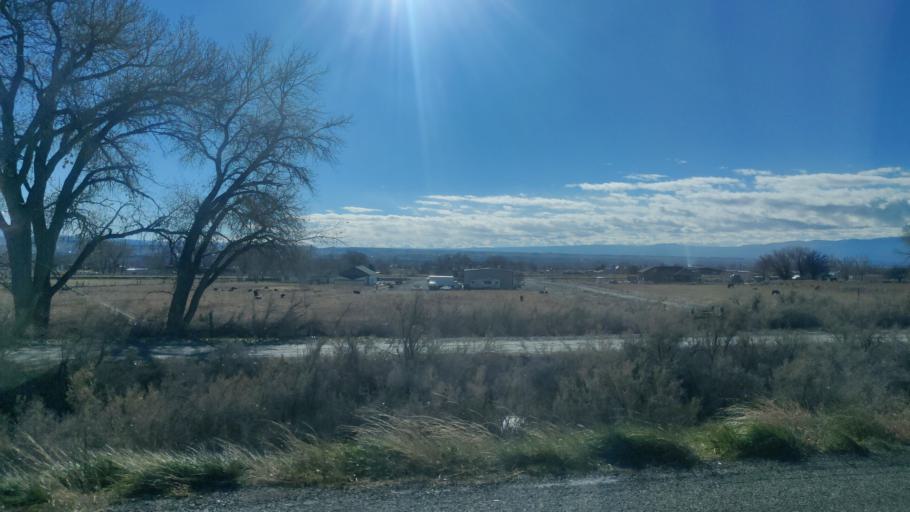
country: US
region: Colorado
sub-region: Mesa County
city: Clifton
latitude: 39.1104
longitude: -108.4182
